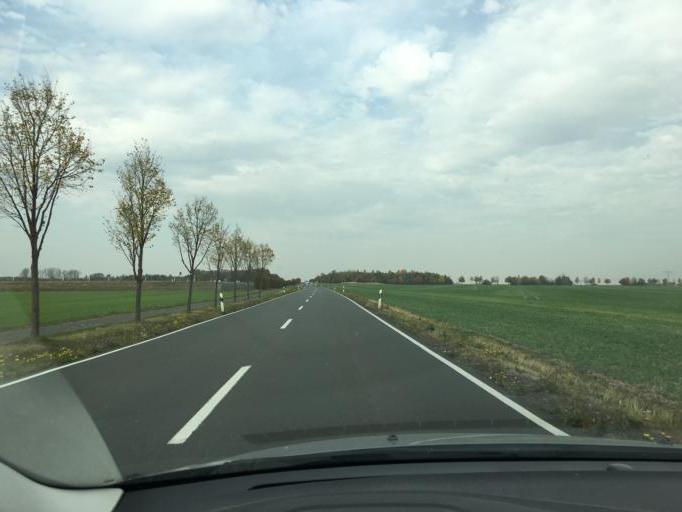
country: DE
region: Saxony
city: Zwochau
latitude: 51.4311
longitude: 12.2841
